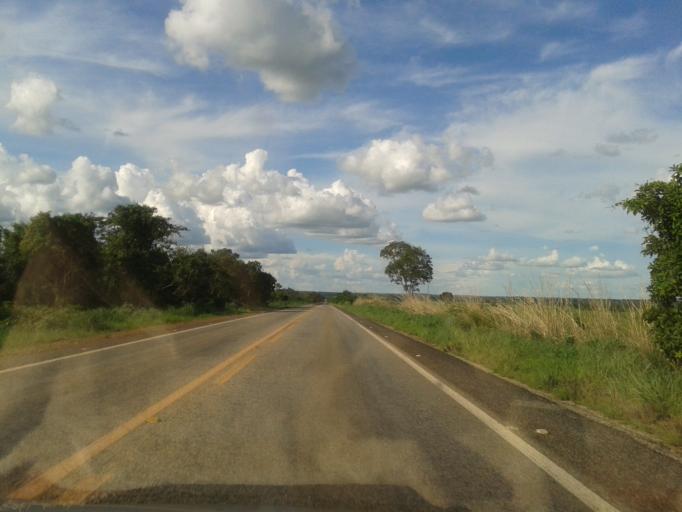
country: BR
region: Goias
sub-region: Mozarlandia
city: Mozarlandia
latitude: -14.5243
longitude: -50.4858
